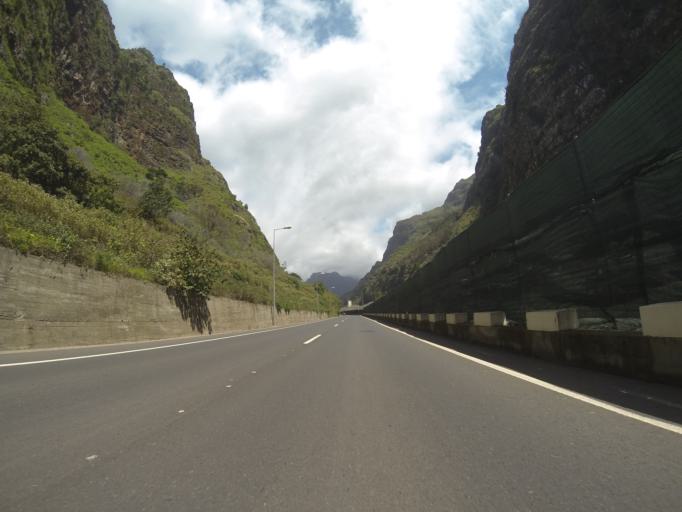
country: PT
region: Madeira
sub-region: Ribeira Brava
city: Campanario
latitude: 32.7059
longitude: -17.0385
